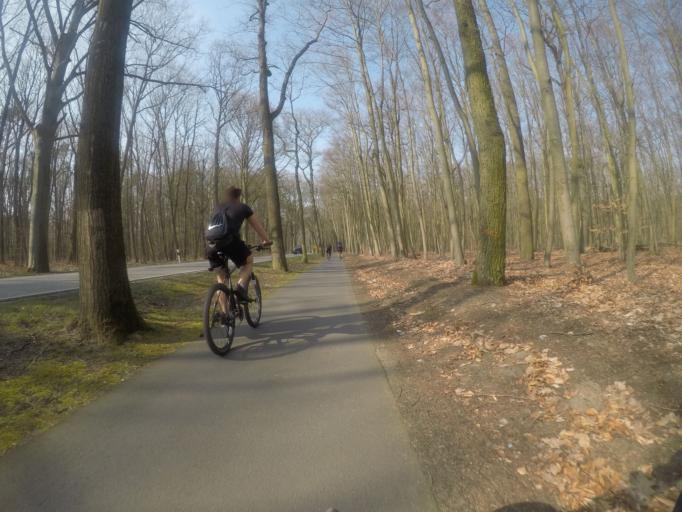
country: DE
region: Brandenburg
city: Konigs Wusterhausen
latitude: 52.2887
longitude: 13.6508
